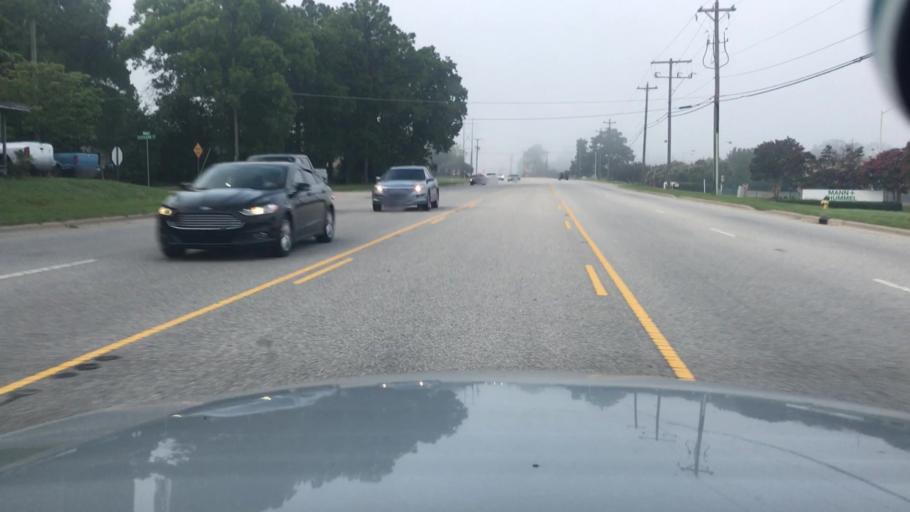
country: US
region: North Carolina
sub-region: Cumberland County
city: Hope Mills
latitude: 35.0138
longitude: -78.9189
